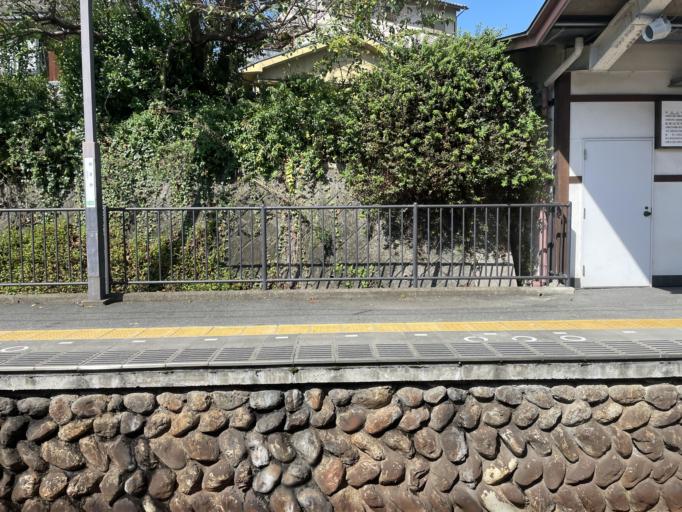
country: JP
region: Nara
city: Kashihara-shi
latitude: 34.4646
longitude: 135.7979
